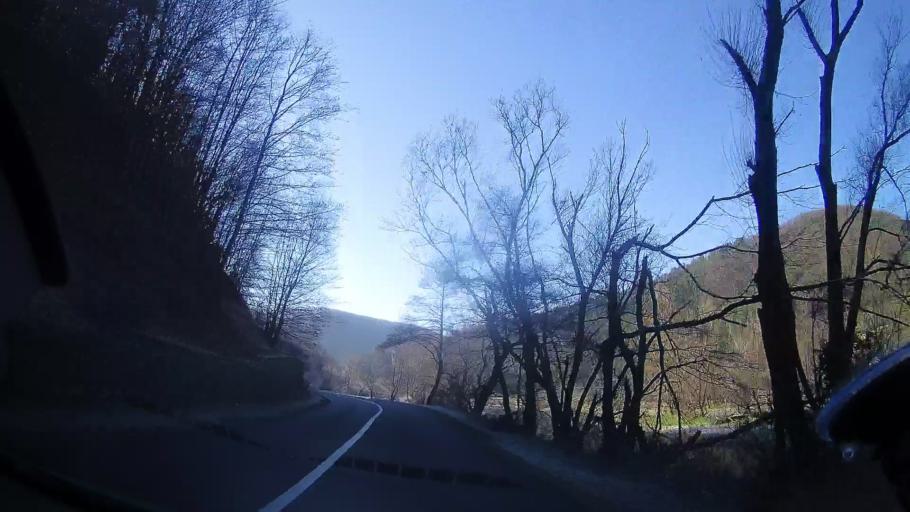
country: RO
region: Bihor
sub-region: Comuna Bulz
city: Bulz
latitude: 46.9314
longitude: 22.6625
